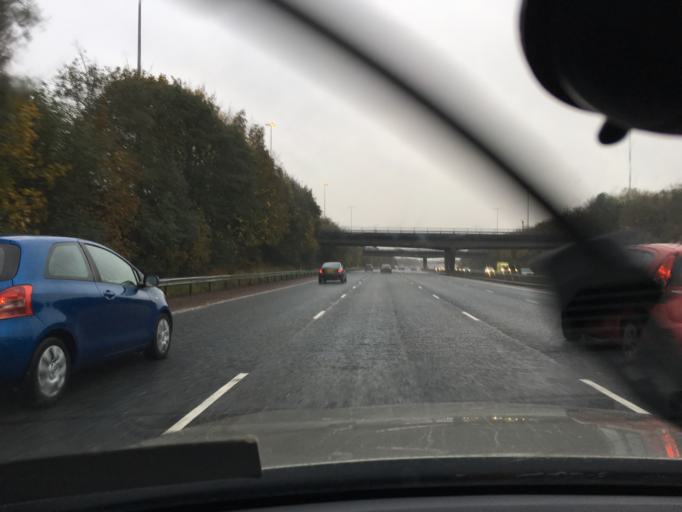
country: GB
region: Northern Ireland
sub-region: Newtownabbey District
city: Newtownabbey
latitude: 54.6313
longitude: -5.9191
